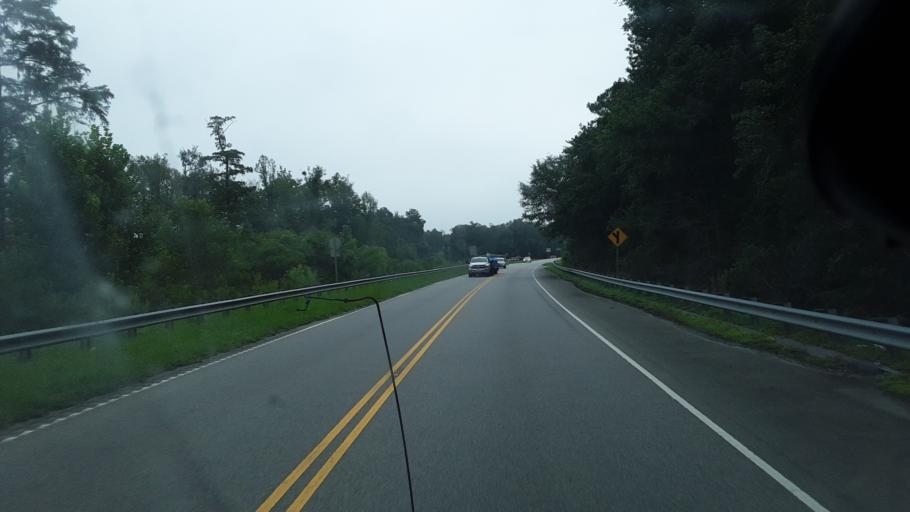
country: US
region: South Carolina
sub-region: Florence County
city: Johnsonville
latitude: 33.9129
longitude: -79.4218
